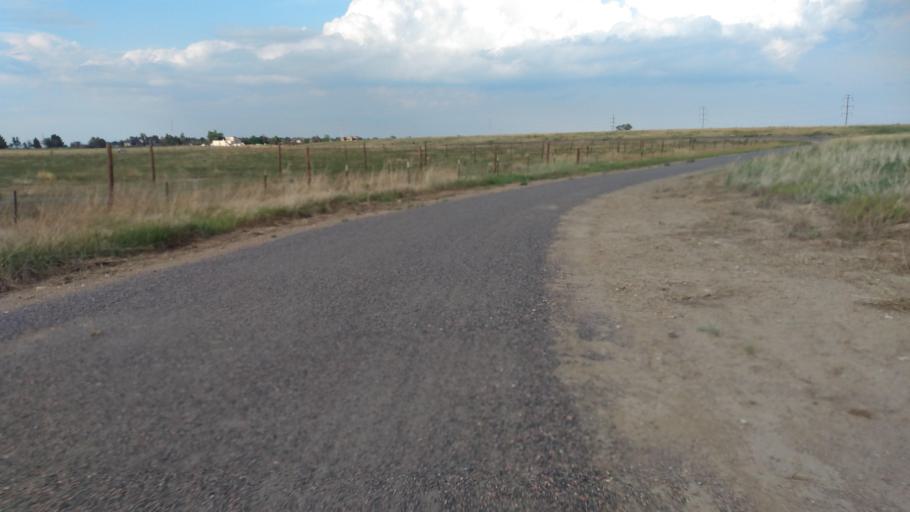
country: US
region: Colorado
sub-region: Boulder County
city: Superior
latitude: 39.9681
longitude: -105.1842
